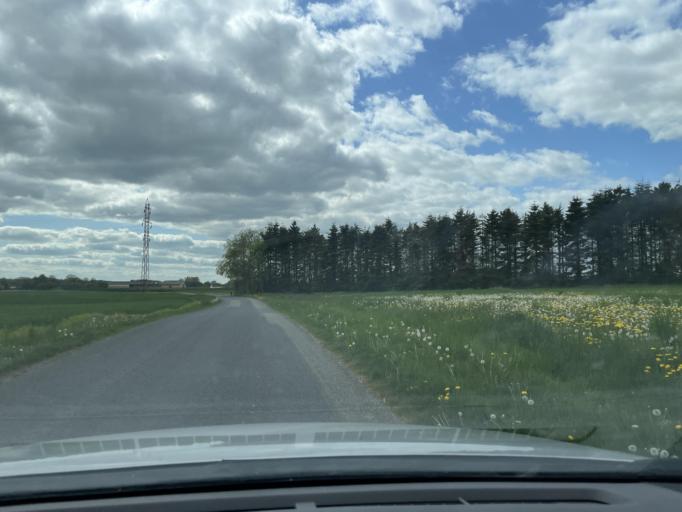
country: DK
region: Central Jutland
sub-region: Skanderborg Kommune
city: Skanderborg
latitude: 55.9239
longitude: 9.9762
